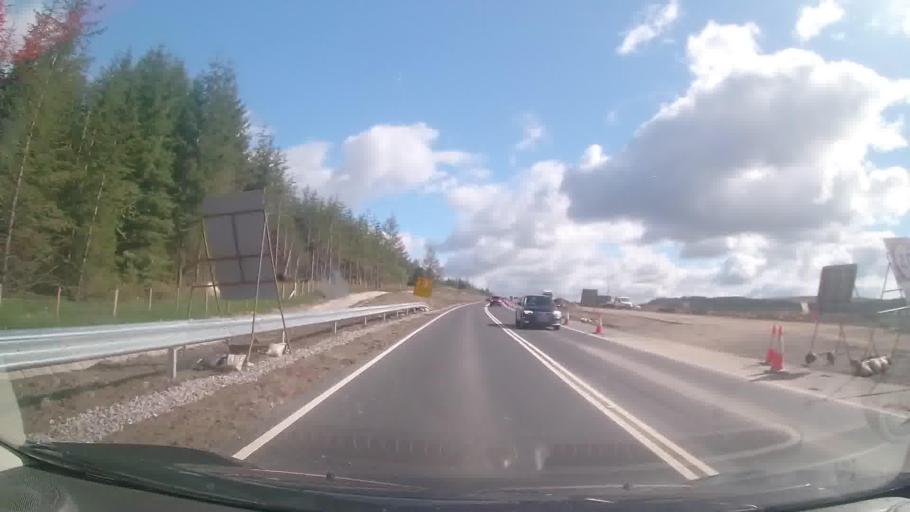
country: GB
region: Wales
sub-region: Rhondda Cynon Taf
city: Aberdare
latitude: 51.7535
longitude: -3.4619
